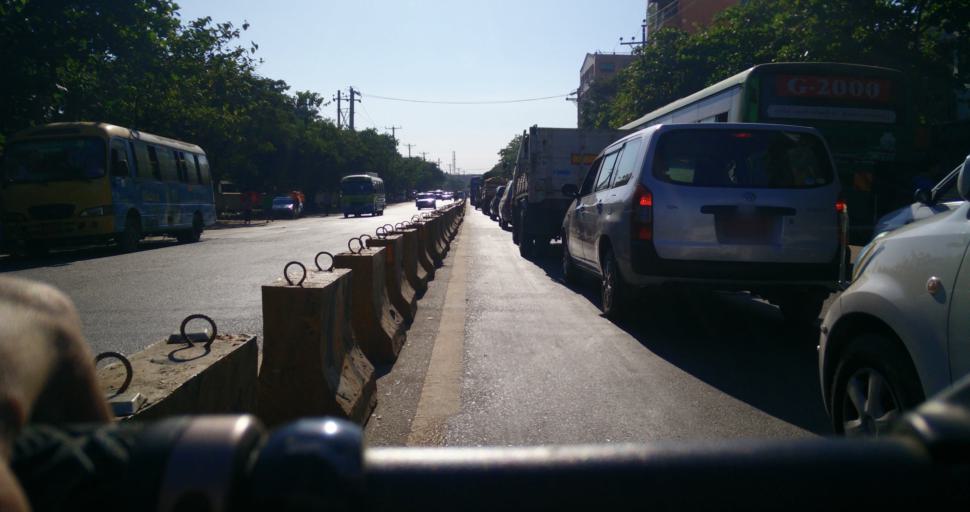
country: MM
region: Yangon
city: Yangon
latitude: 16.8455
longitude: 96.2013
